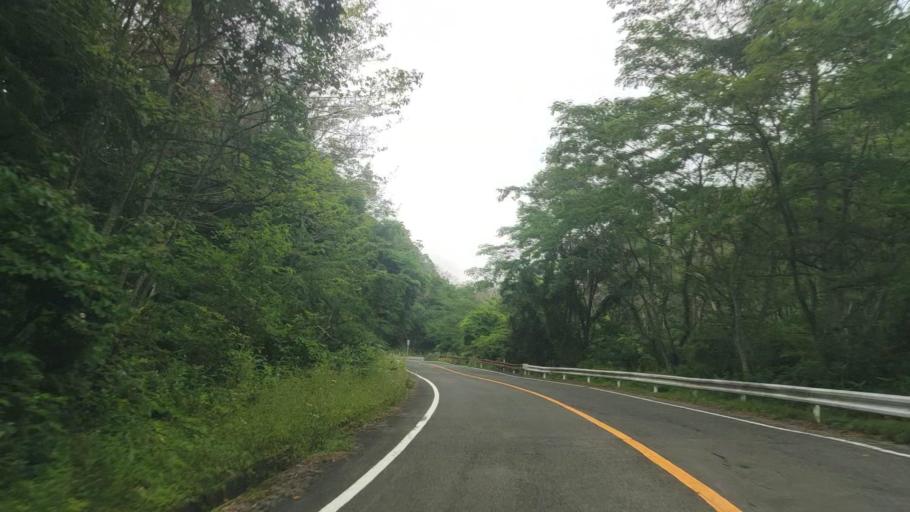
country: JP
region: Tottori
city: Kurayoshi
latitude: 35.3036
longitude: 133.6220
